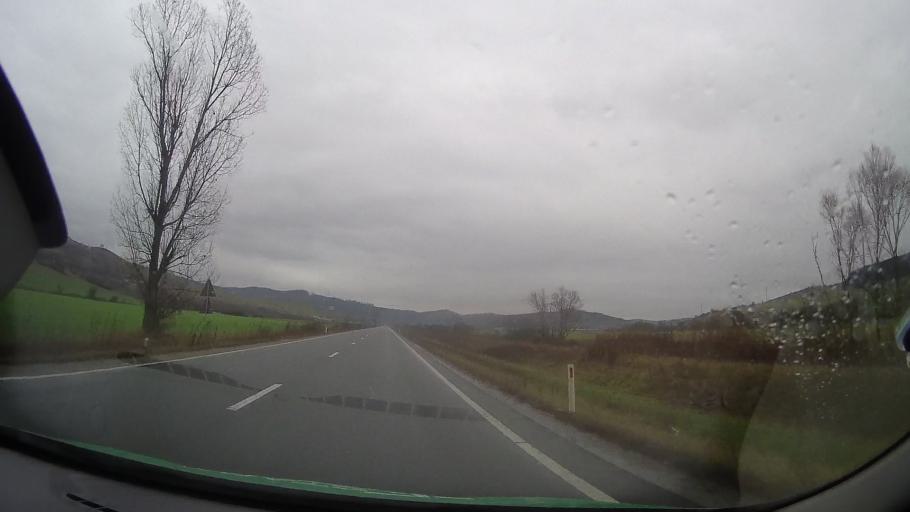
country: RO
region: Bistrita-Nasaud
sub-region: Comuna Teaca
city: Teaca
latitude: 46.9278
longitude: 24.4846
